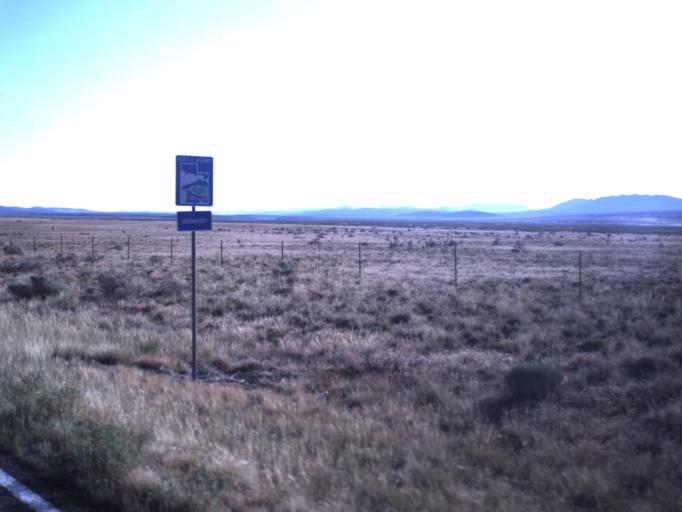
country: US
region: Utah
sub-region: Iron County
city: Enoch
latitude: 37.8916
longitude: -113.0316
